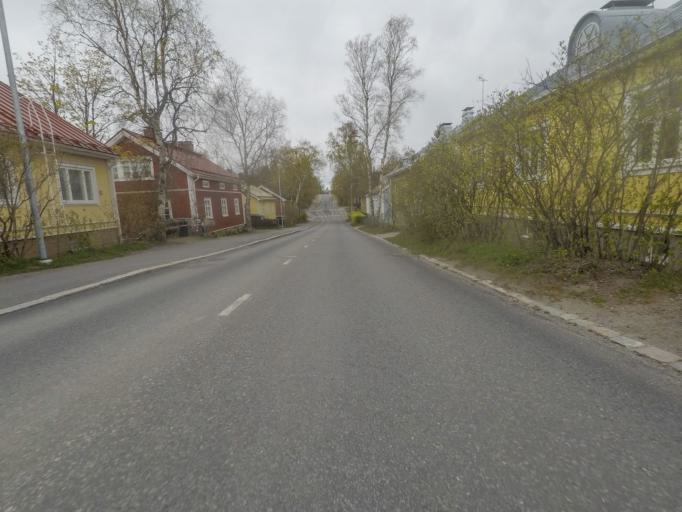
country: FI
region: Pirkanmaa
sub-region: Tampere
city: Tampere
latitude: 61.4839
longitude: 23.7882
